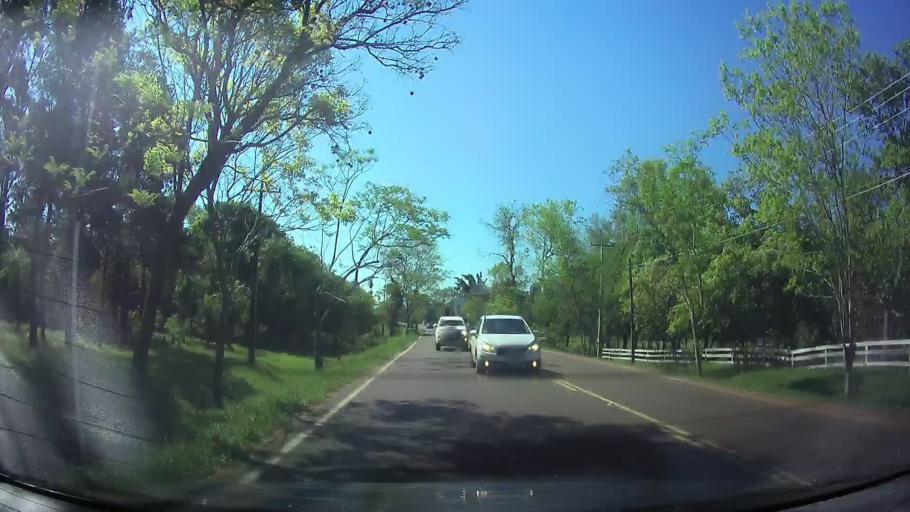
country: PY
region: Cordillera
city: San Bernardino
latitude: -25.3545
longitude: -57.2676
